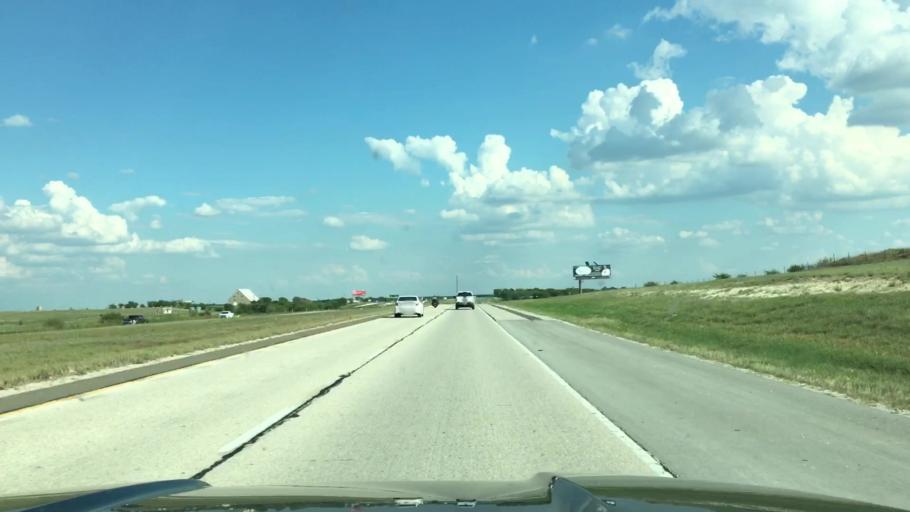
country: US
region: Texas
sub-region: Wise County
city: Boyd
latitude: 33.1552
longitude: -97.5173
